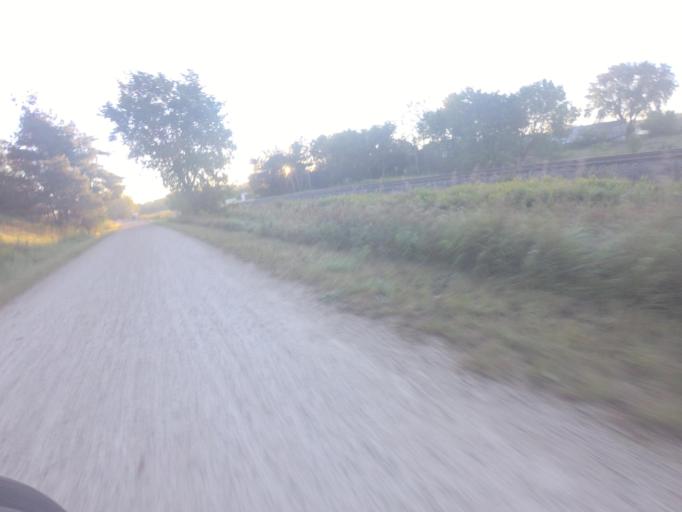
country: CA
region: Ontario
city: Bradford West Gwillimbury
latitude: 43.9676
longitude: -79.8134
